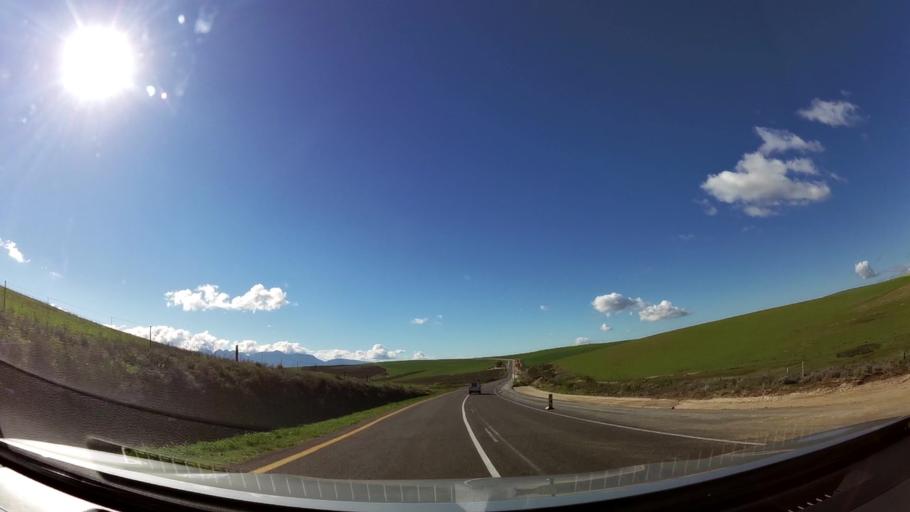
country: ZA
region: Western Cape
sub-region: Overberg District Municipality
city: Caledon
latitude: -34.1991
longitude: 19.6248
